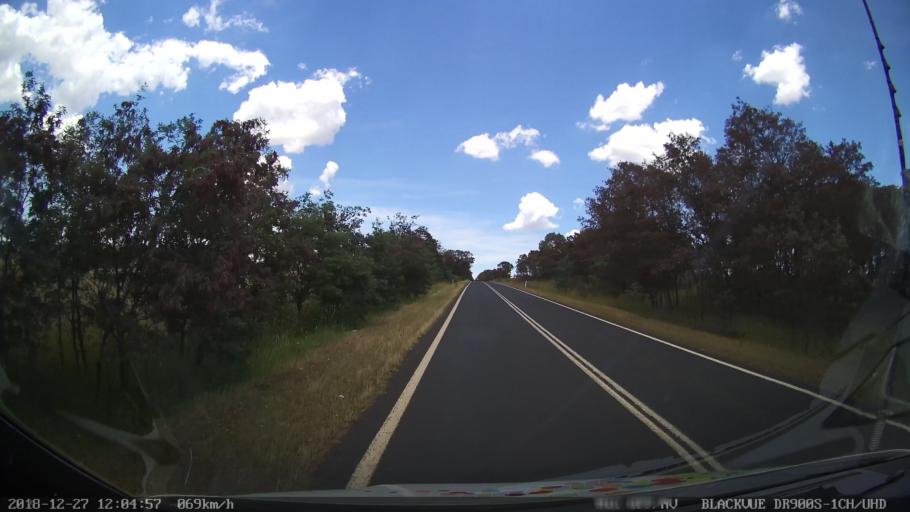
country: AU
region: New South Wales
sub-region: Blayney
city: Blayney
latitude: -33.7995
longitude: 149.3438
